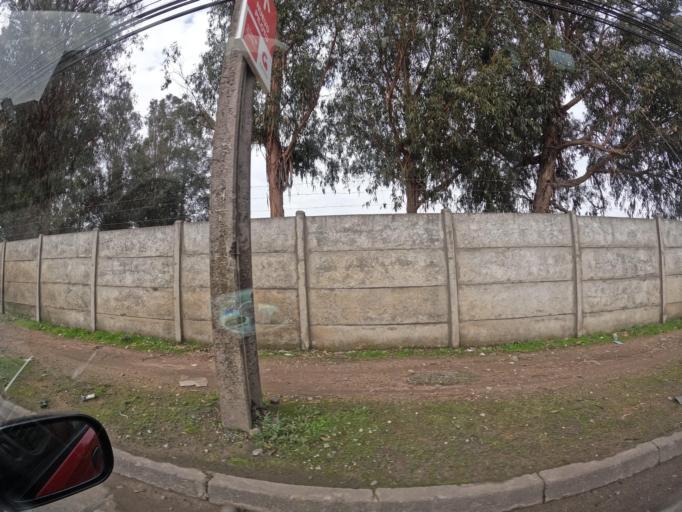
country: CL
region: Maule
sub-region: Provincia de Linares
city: Linares
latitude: -35.8388
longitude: -71.5944
